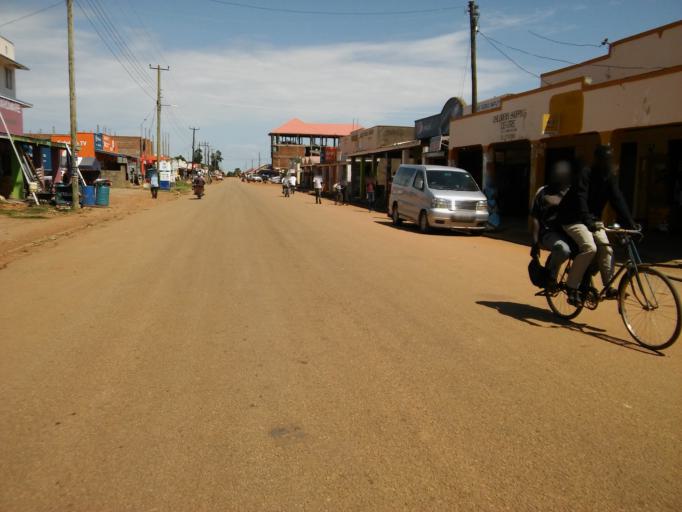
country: UG
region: Eastern Region
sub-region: Kumi District
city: Kumi
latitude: 1.4873
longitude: 33.9323
